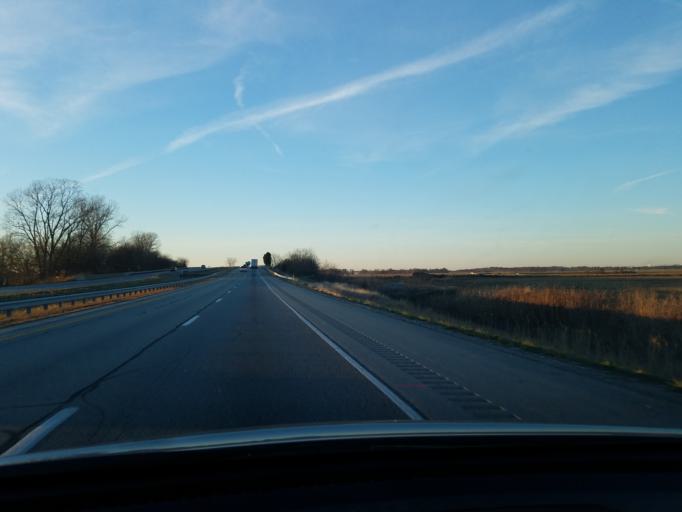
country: US
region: Indiana
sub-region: Posey County
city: Poseyville
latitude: 38.1790
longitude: -87.7613
